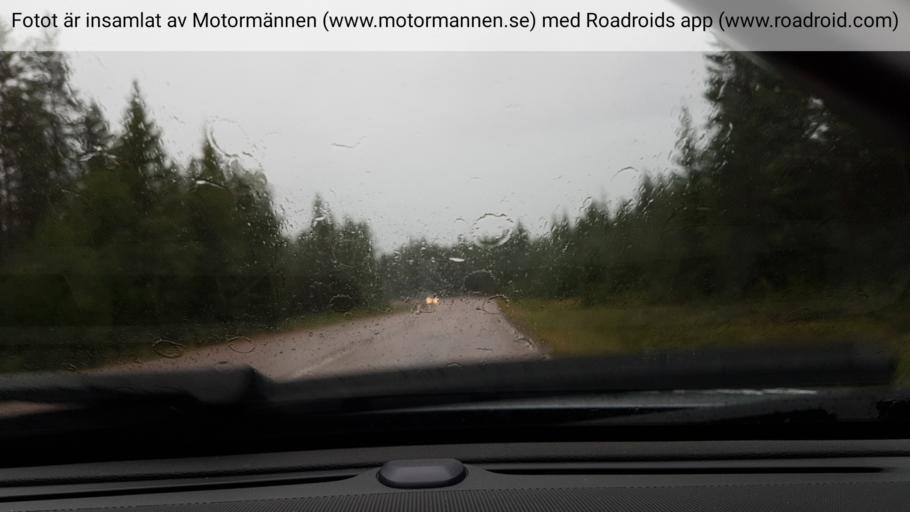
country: SE
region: Dalarna
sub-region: Faluns Kommun
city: Bjursas
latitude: 60.8373
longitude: 15.3446
